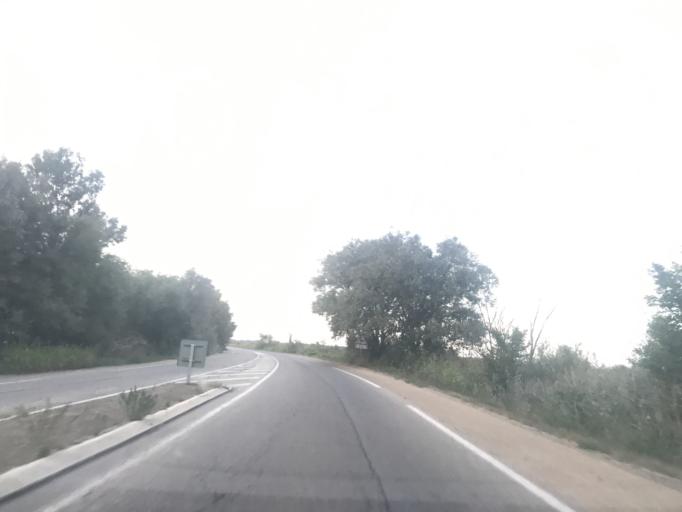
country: FR
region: Provence-Alpes-Cote d'Azur
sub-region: Departement des Bouches-du-Rhone
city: Saintes-Maries-de-la-Mer
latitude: 43.5279
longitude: 4.4013
